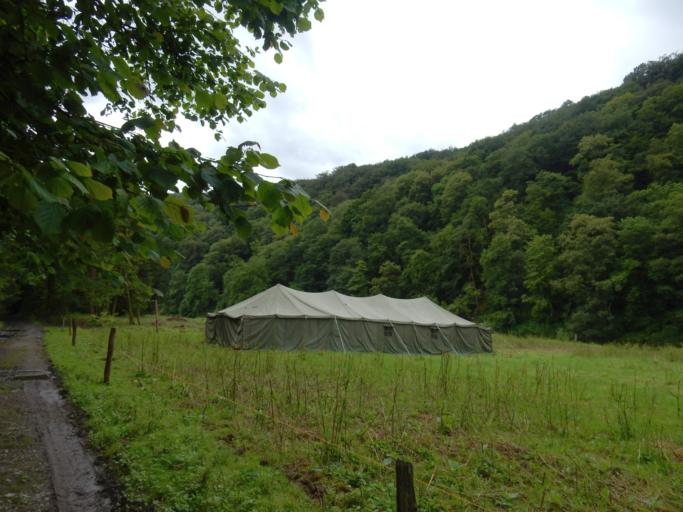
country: FR
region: Champagne-Ardenne
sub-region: Departement des Ardennes
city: Les Hautes-Rivieres
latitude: 49.8564
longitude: 4.9335
